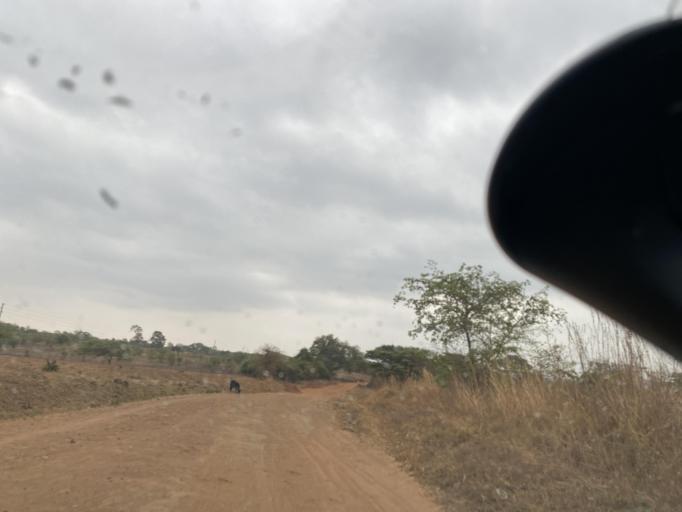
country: ZM
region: Lusaka
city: Chongwe
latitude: -15.1650
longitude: 28.7621
